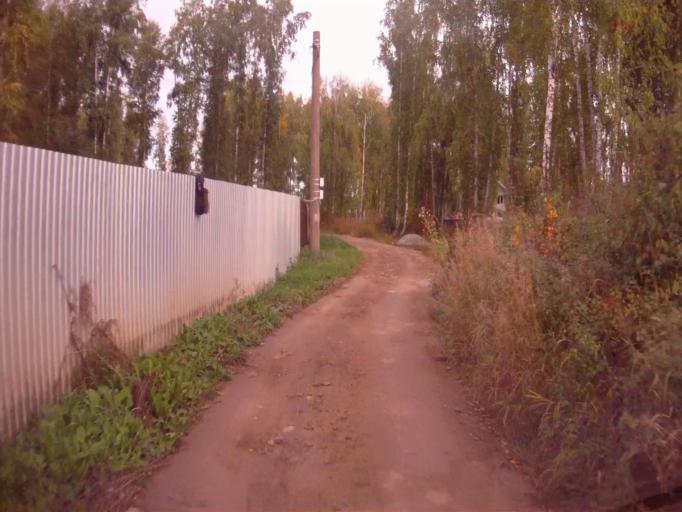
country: RU
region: Chelyabinsk
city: Sargazy
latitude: 55.1277
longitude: 61.2504
